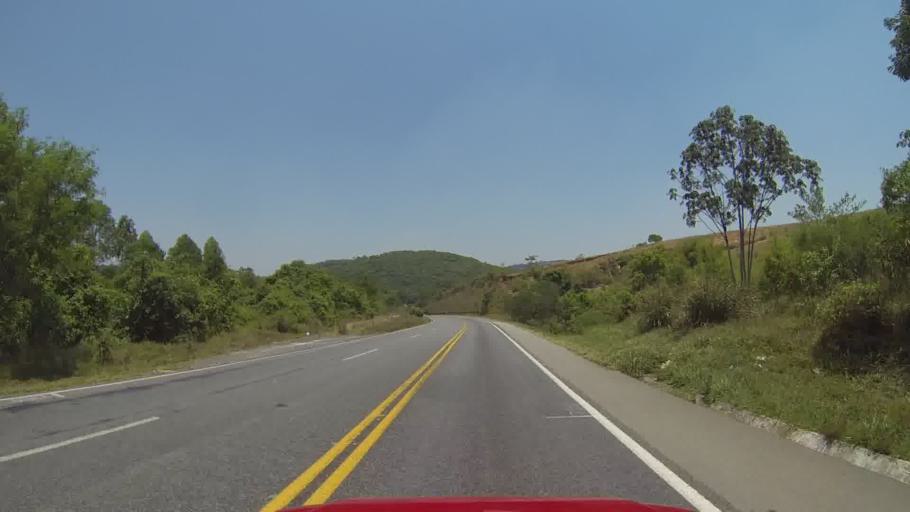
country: BR
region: Minas Gerais
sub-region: Itapecerica
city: Itapecerica
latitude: -20.2821
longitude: -45.1443
